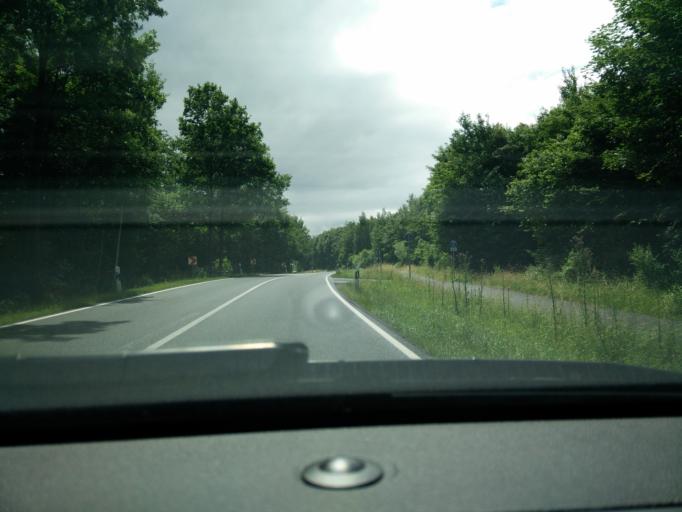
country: DE
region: Saxony
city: Grossbardau
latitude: 51.1704
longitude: 12.6797
